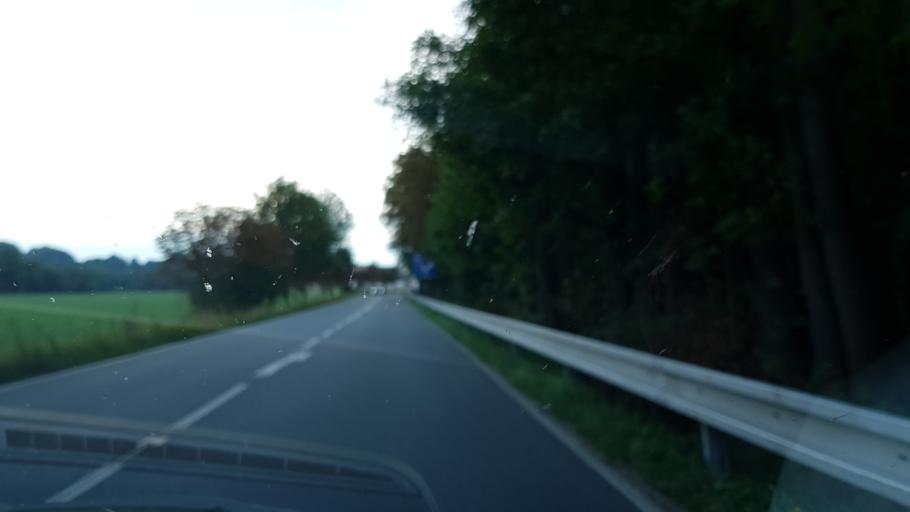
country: CZ
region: Pardubicky
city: Zamberk
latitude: 50.0839
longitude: 16.4795
